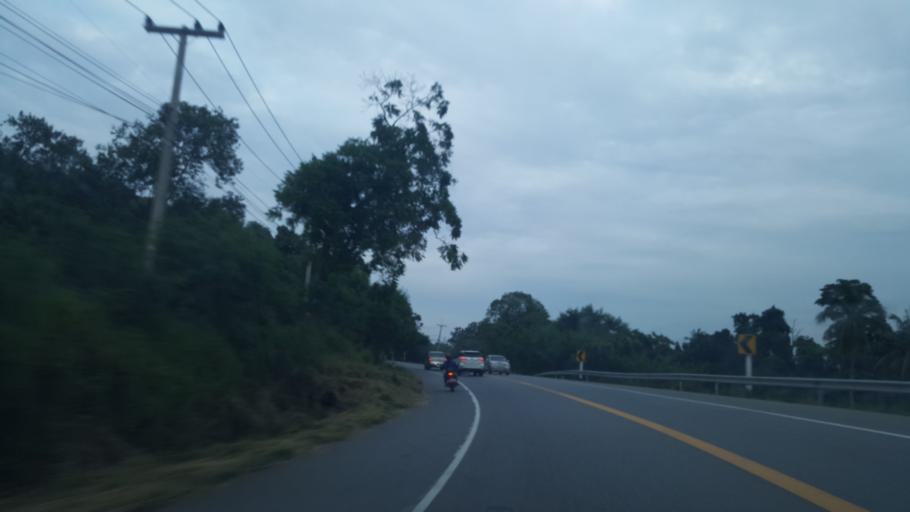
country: TH
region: Chon Buri
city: Ban Talat Bueng
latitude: 12.9581
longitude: 101.0168
